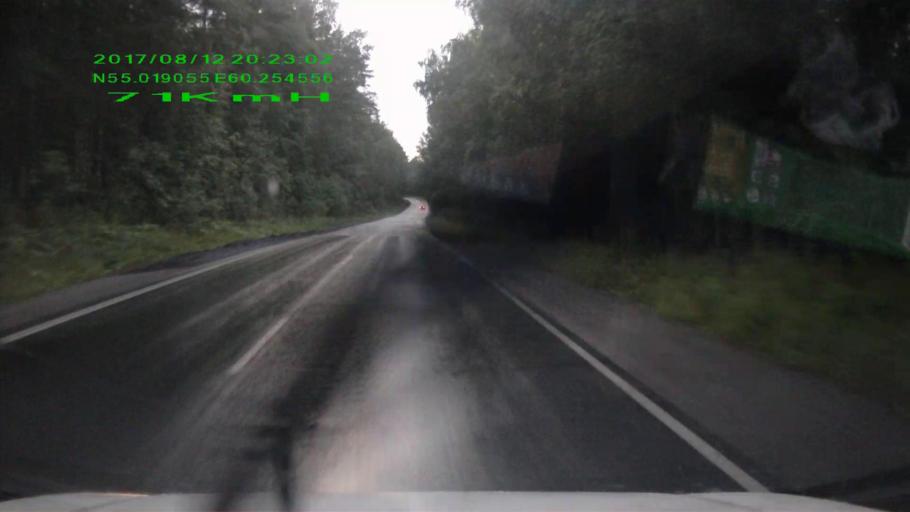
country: RU
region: Chelyabinsk
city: Chebarkul'
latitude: 55.0194
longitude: 60.2543
